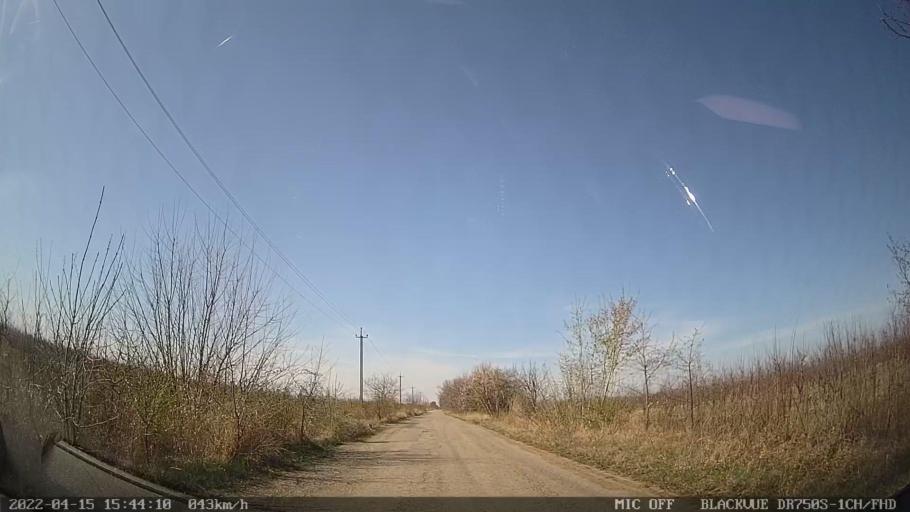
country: MD
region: Raionul Ocnita
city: Otaci
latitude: 48.3688
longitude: 27.9235
